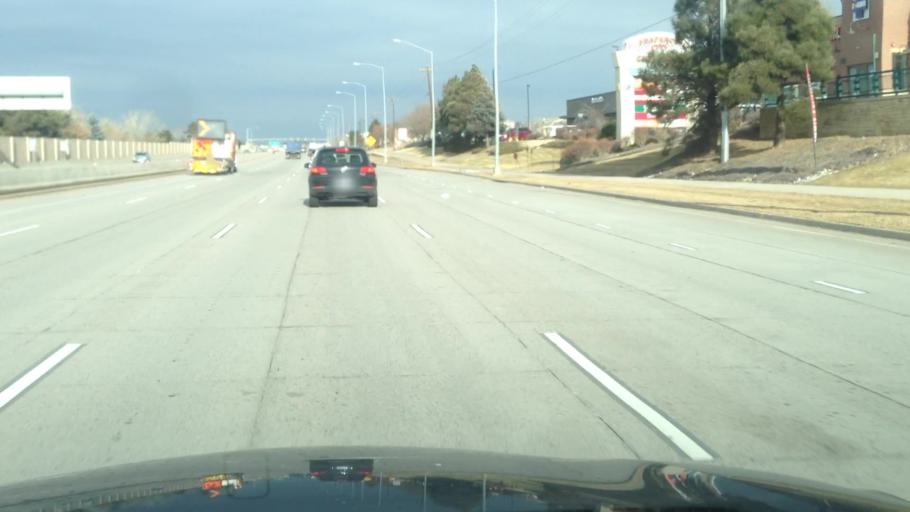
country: US
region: Colorado
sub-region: Arapahoe County
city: Dove Valley
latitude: 39.5981
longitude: -104.8038
